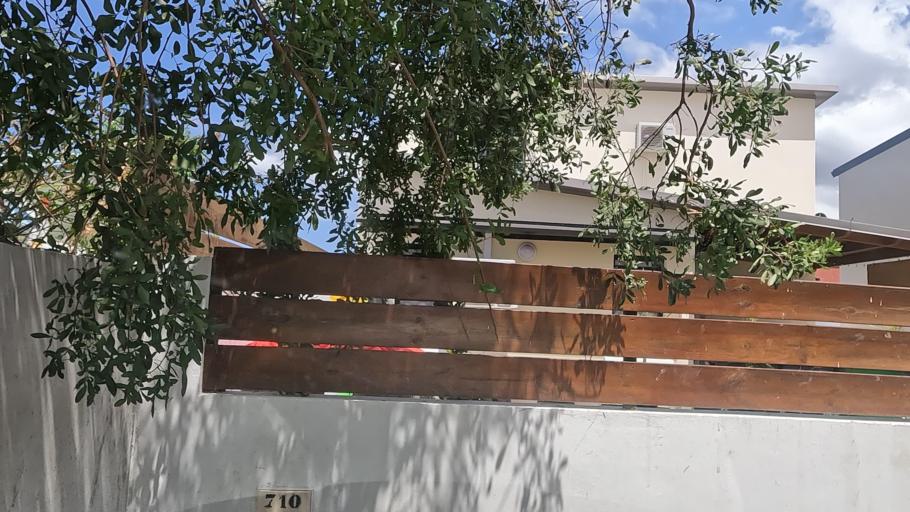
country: RE
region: Reunion
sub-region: Reunion
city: Saint-Louis
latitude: -21.2795
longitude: 55.4426
